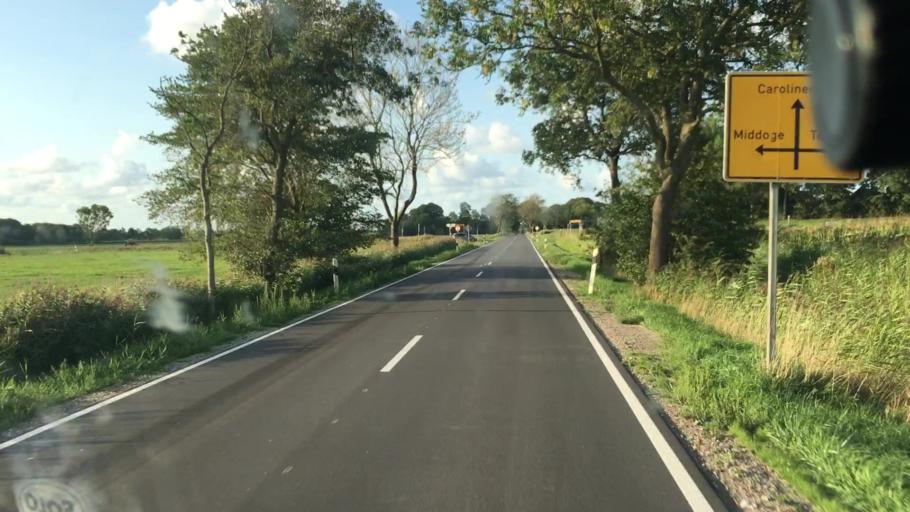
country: DE
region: Lower Saxony
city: Jever
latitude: 53.6369
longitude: 7.8611
